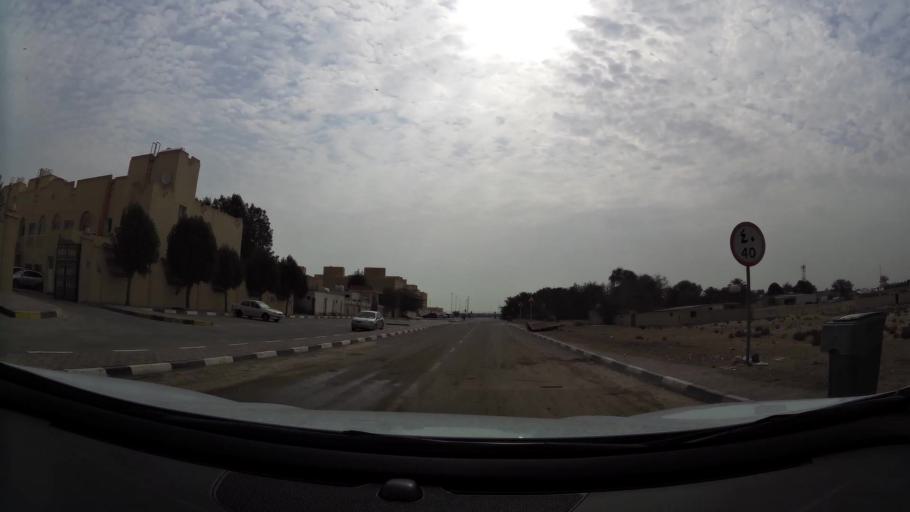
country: AE
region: Abu Dhabi
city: Abu Dhabi
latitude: 24.6876
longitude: 54.7669
